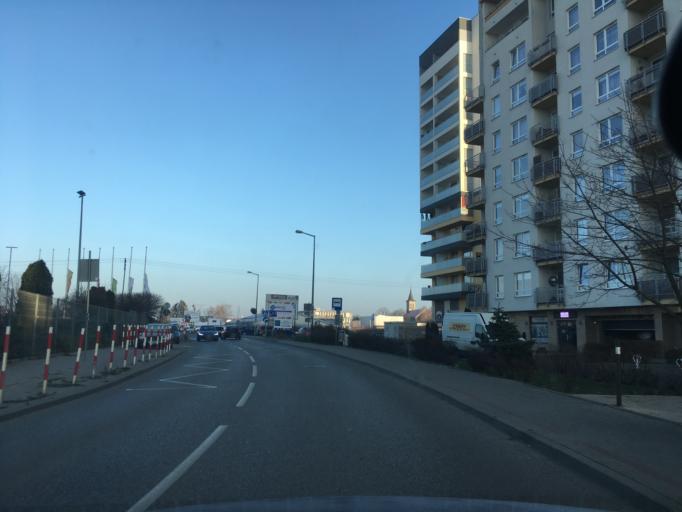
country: PL
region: Masovian Voivodeship
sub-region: Powiat piaseczynski
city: Piaseczno
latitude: 52.0796
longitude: 21.0085
